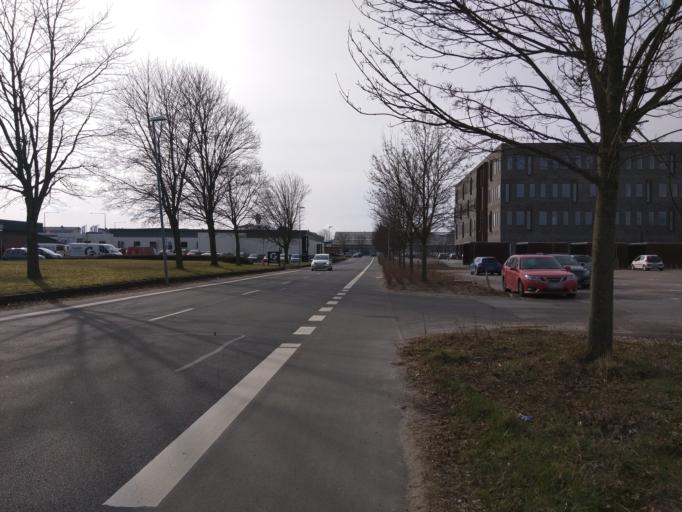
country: DK
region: Central Jutland
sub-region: Silkeborg Kommune
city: Silkeborg
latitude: 56.1874
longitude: 9.5613
